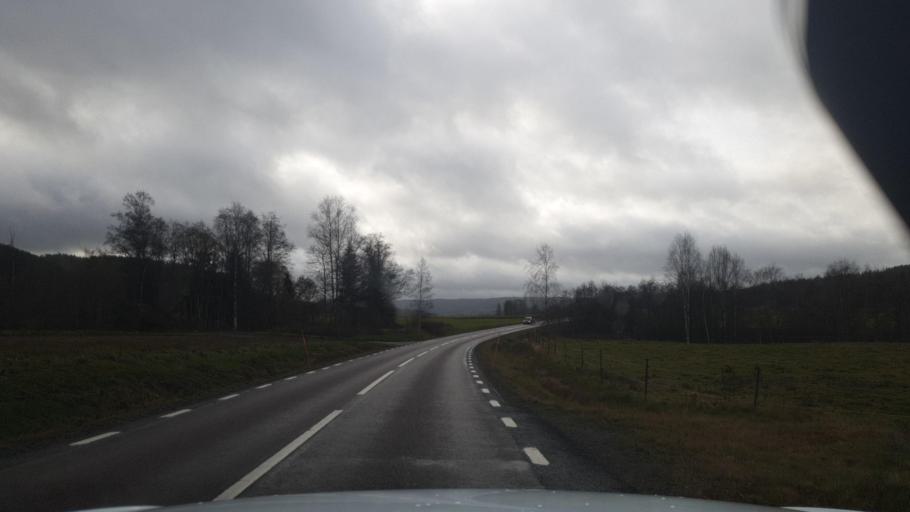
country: SE
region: Vaermland
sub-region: Eda Kommun
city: Amotfors
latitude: 59.6621
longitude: 12.1457
